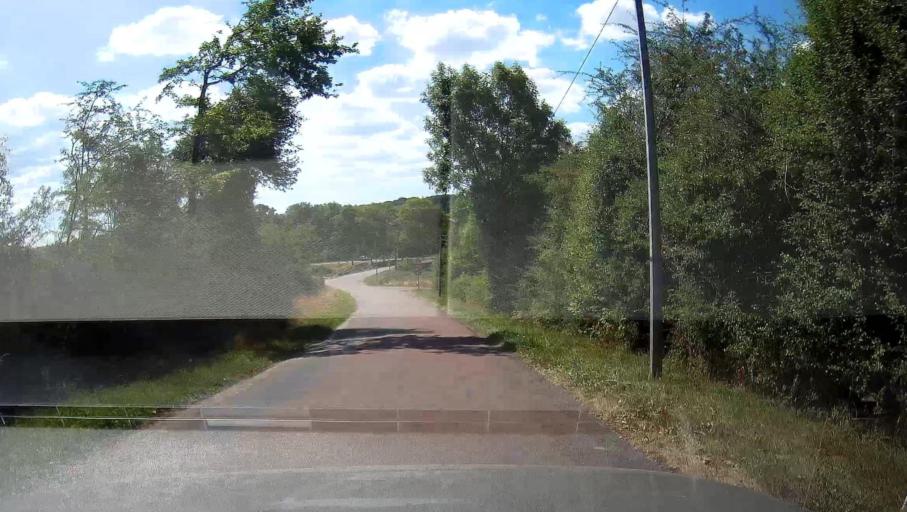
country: FR
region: Champagne-Ardenne
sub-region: Departement de la Haute-Marne
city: Langres
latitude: 47.8738
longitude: 5.3561
